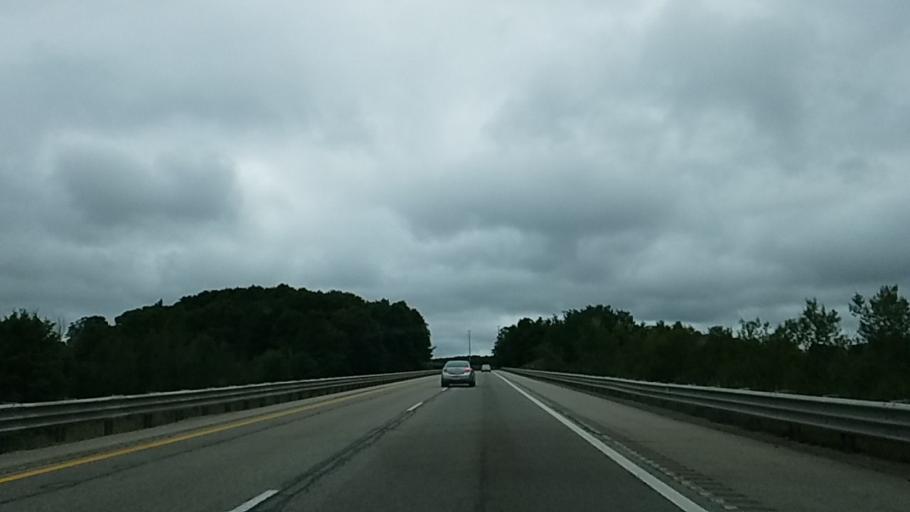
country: US
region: Michigan
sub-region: Otsego County
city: Gaylord
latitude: 45.1169
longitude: -84.6805
